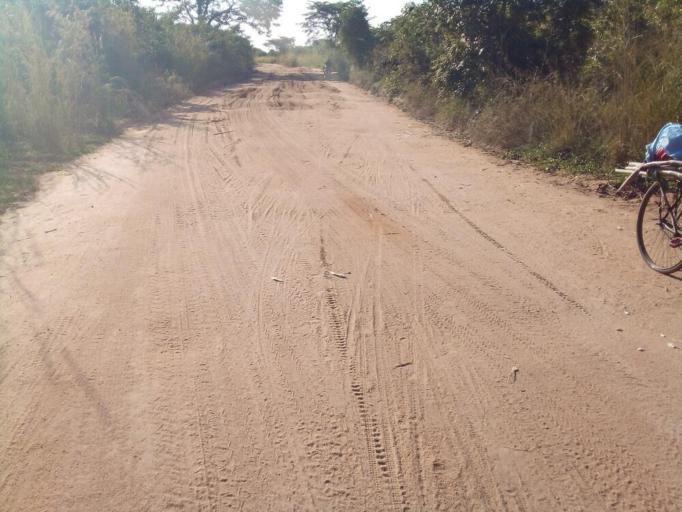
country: MZ
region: Zambezia
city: Quelimane
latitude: -17.5085
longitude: 36.8308
